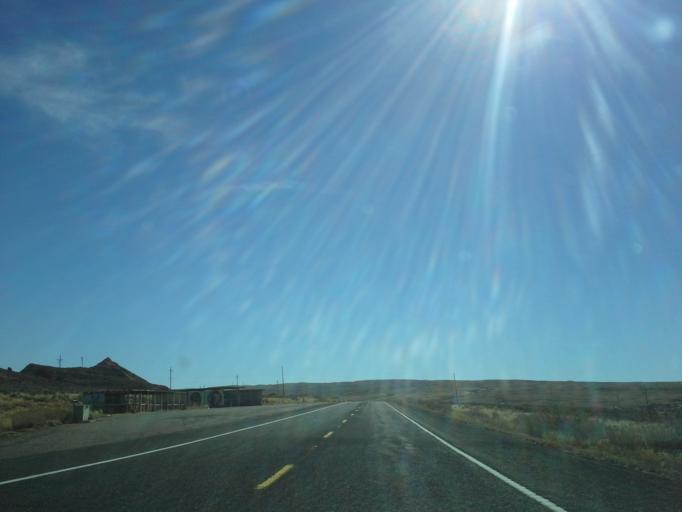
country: US
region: Arizona
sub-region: Coconino County
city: LeChee
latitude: 36.6172
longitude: -111.6545
